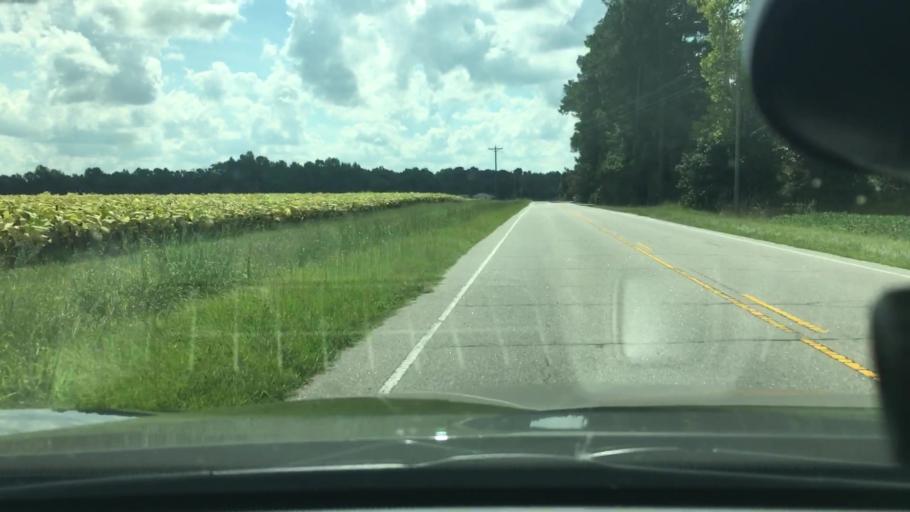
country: US
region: North Carolina
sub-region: Edgecombe County
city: Pinetops
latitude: 35.7509
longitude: -77.5448
